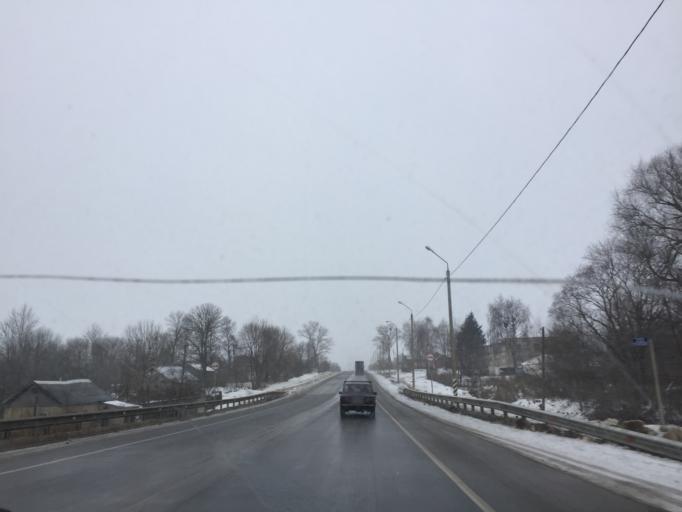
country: RU
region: Tula
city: Plavsk
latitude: 53.8128
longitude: 37.3923
